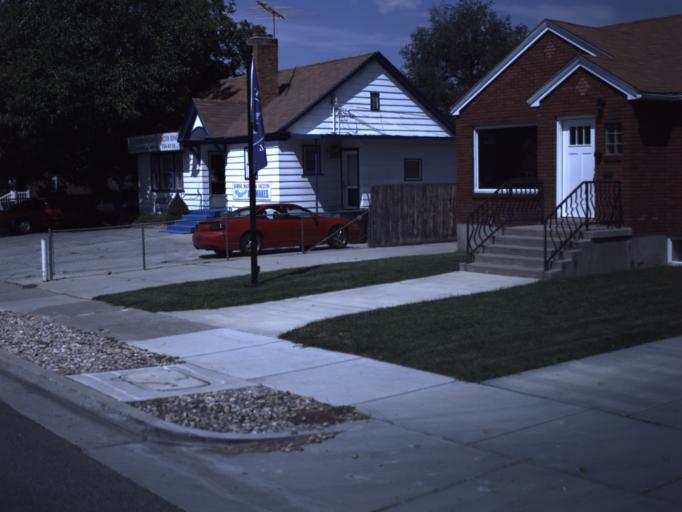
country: US
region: Utah
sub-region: Utah County
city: American Fork
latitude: 40.3769
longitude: -111.8090
